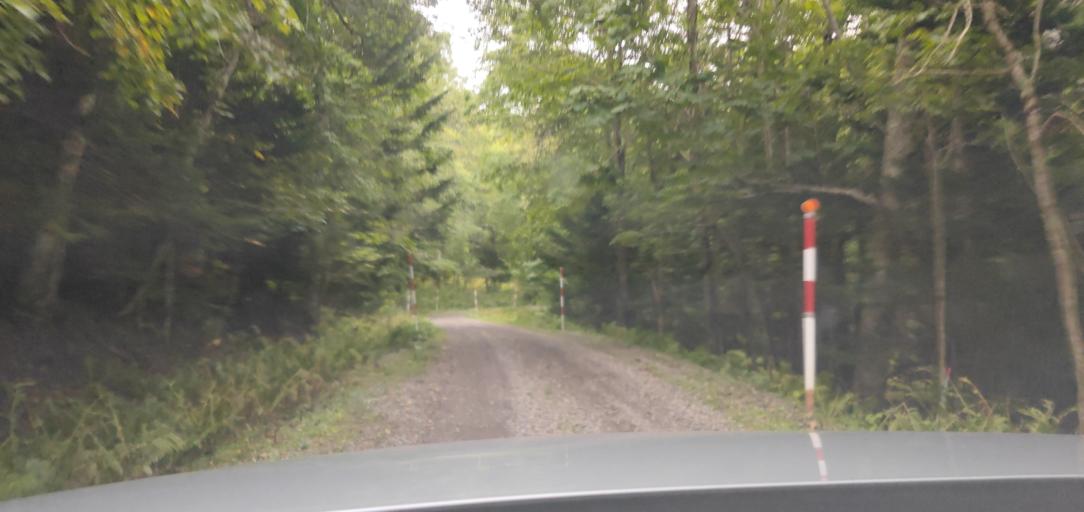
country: JP
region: Hokkaido
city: Kitami
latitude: 43.3690
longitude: 143.9400
